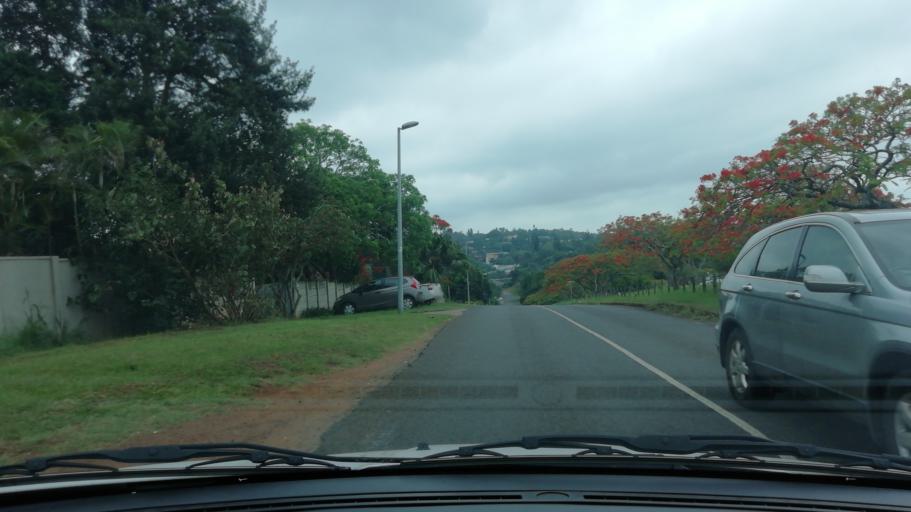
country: ZA
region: KwaZulu-Natal
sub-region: uThungulu District Municipality
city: Empangeni
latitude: -28.7628
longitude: 31.8917
